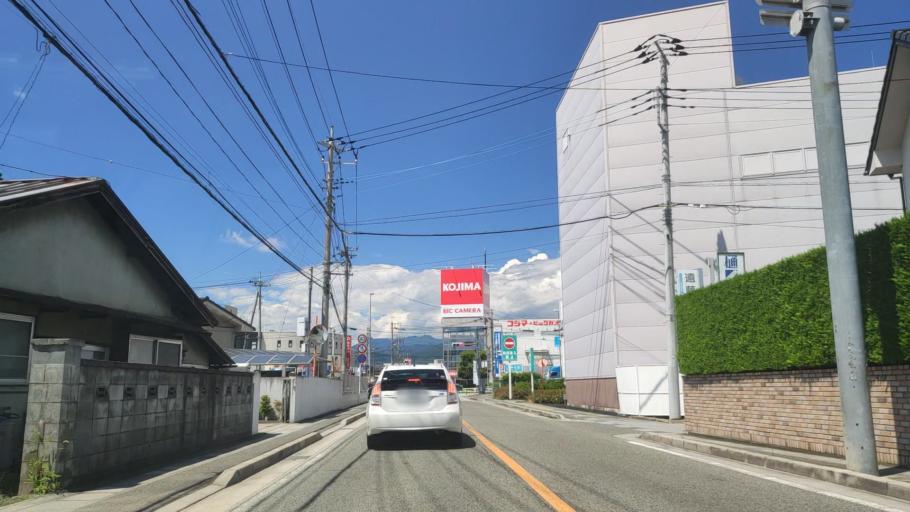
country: JP
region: Yamanashi
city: Kofu-shi
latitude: 35.6322
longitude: 138.5713
